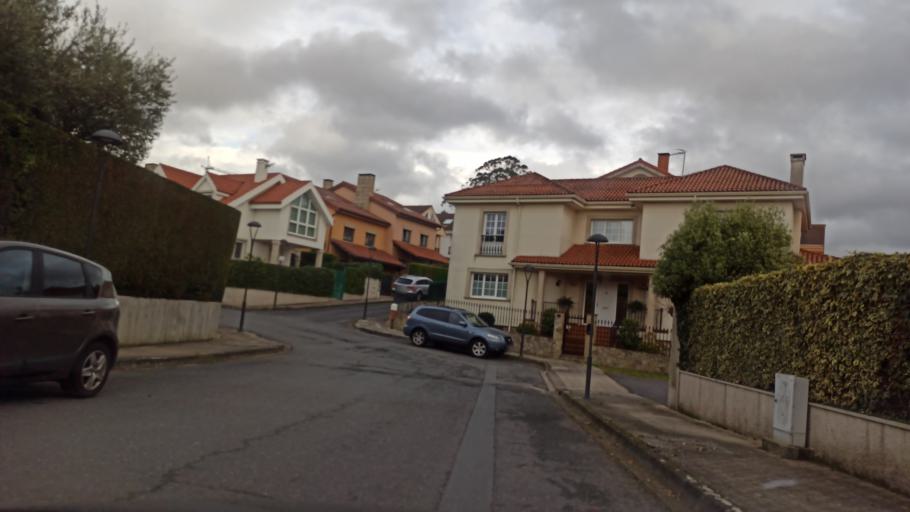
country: ES
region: Galicia
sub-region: Provincia da Coruna
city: Cambre
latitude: 43.3238
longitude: -8.3489
